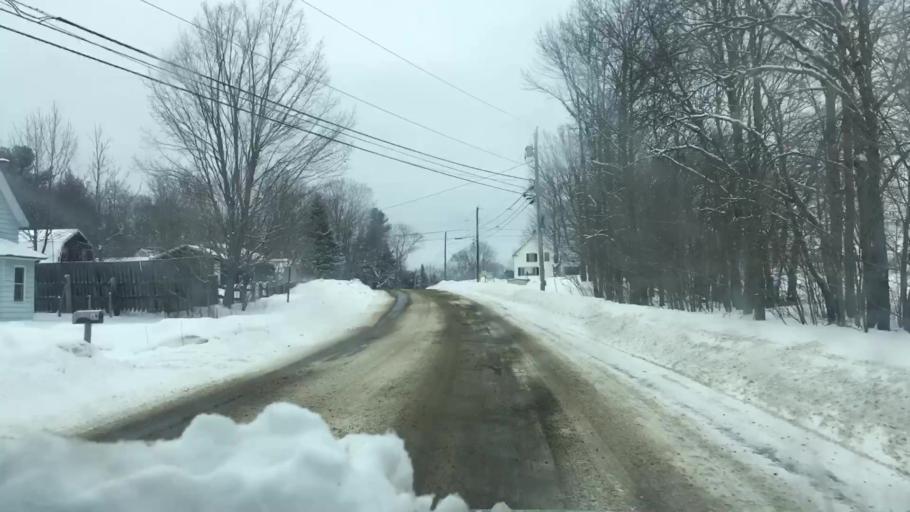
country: US
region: Maine
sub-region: Penobscot County
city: Bradford
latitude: 45.0106
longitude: -68.9992
